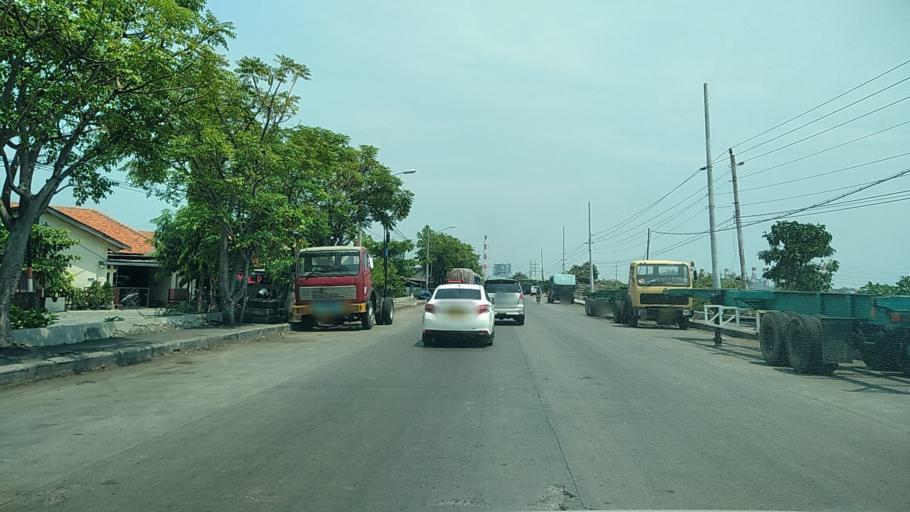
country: ID
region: Central Java
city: Semarang
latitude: -6.9618
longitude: 110.4309
